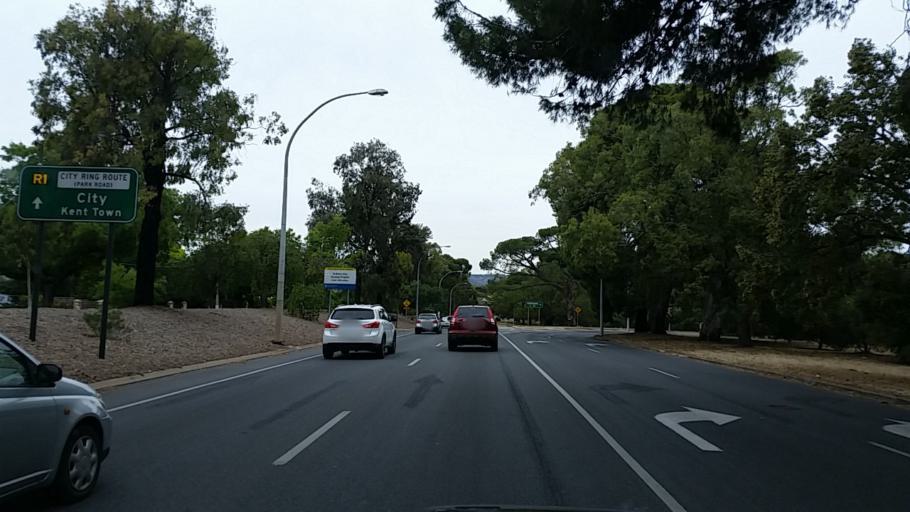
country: AU
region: South Australia
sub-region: Adelaide
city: North Adelaide
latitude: -34.9035
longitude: 138.6112
